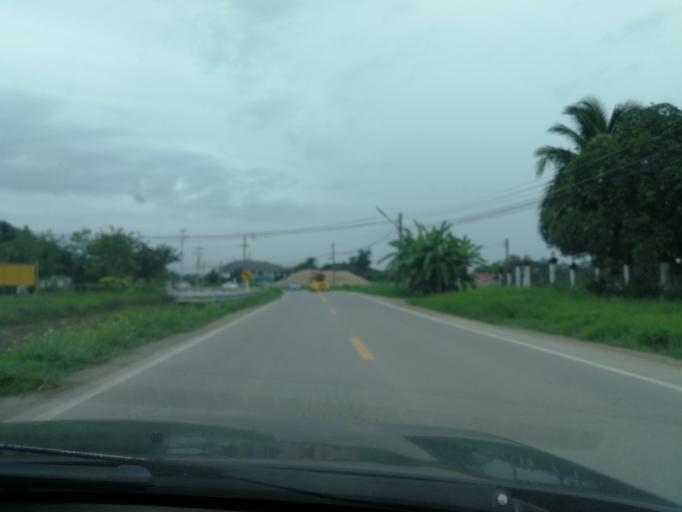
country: TH
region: Chiang Mai
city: San Pa Tong
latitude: 18.6234
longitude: 98.8974
